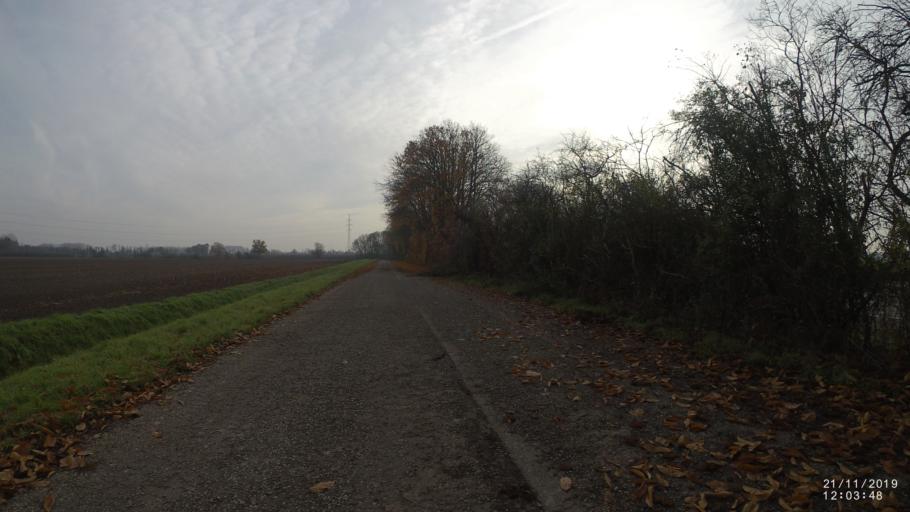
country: BE
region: Flanders
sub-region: Provincie Limburg
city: Sint-Truiden
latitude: 50.8326
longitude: 5.2226
